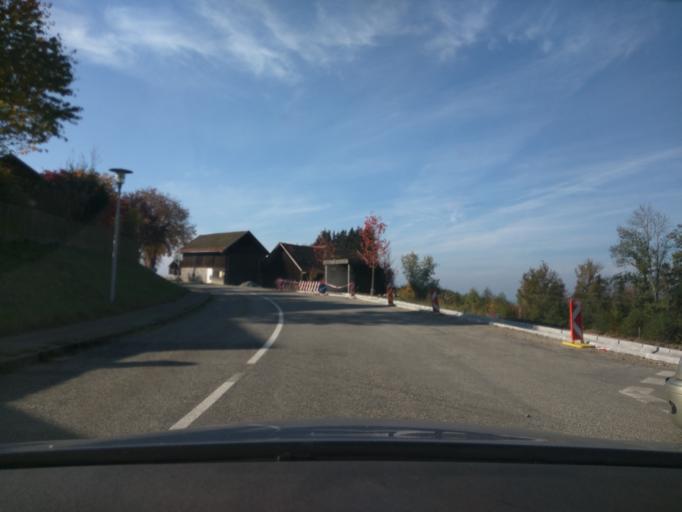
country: DE
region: Bavaria
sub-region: Lower Bavaria
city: Thyrnau
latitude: 48.5654
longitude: 13.5255
